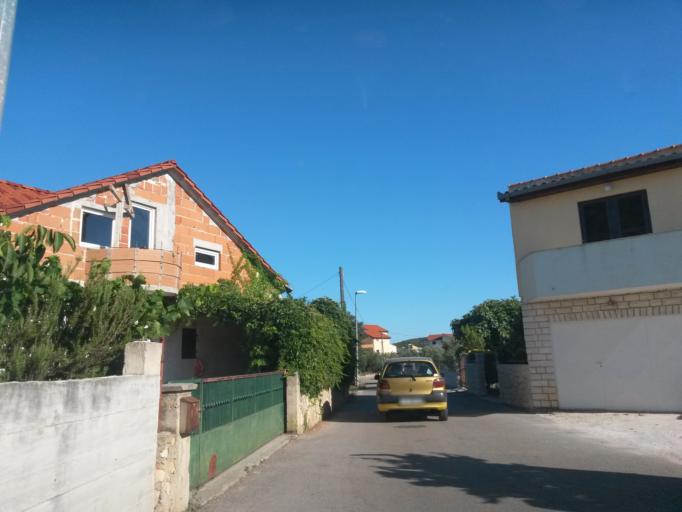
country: HR
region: Sibensko-Kniniska
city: Rogoznica
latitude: 43.5385
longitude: 15.9613
